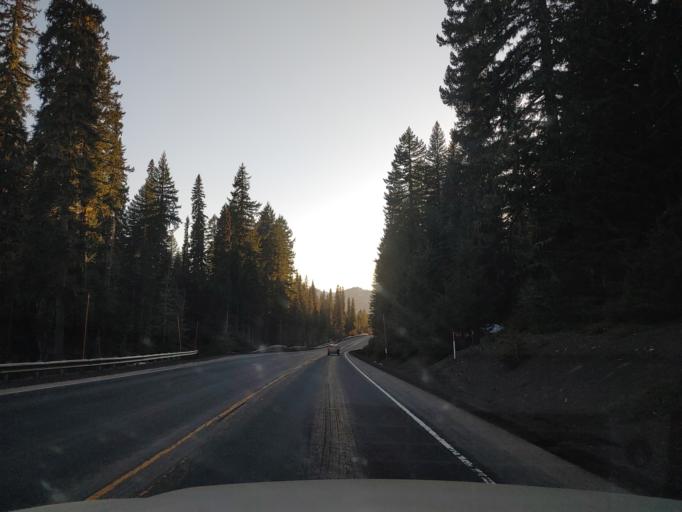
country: US
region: Oregon
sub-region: Lane County
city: Oakridge
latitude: 43.6184
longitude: -122.0790
